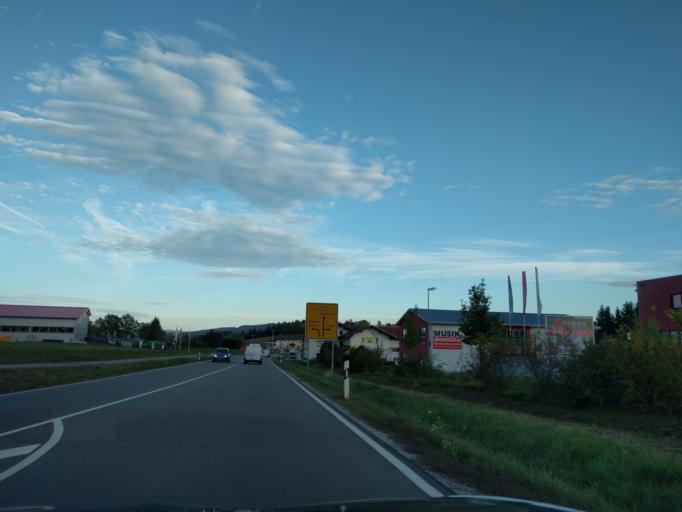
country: DE
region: Bavaria
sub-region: Lower Bavaria
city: Patersdorf
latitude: 49.0269
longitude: 12.9692
